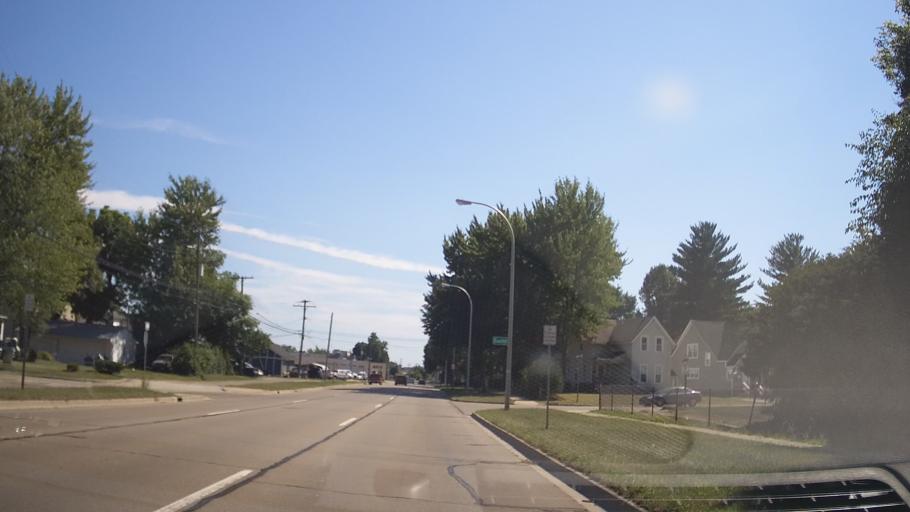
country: US
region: Michigan
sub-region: Macomb County
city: Mount Clemens
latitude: 42.6076
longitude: -82.8733
